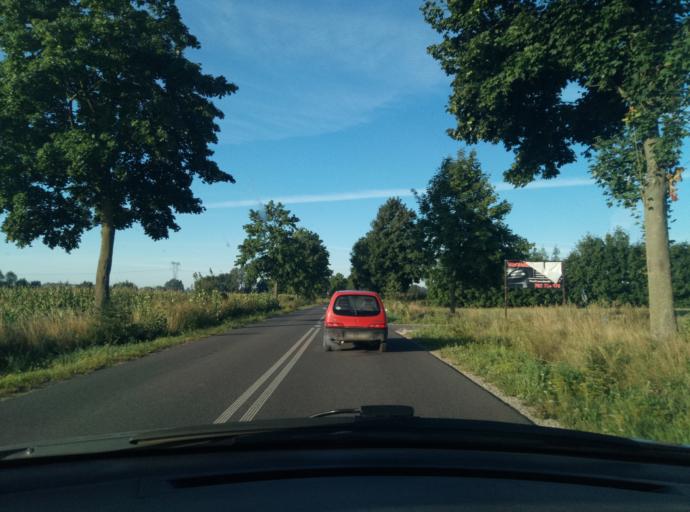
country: PL
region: Kujawsko-Pomorskie
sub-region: Powiat wabrzeski
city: Wabrzezno
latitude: 53.2224
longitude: 18.9463
